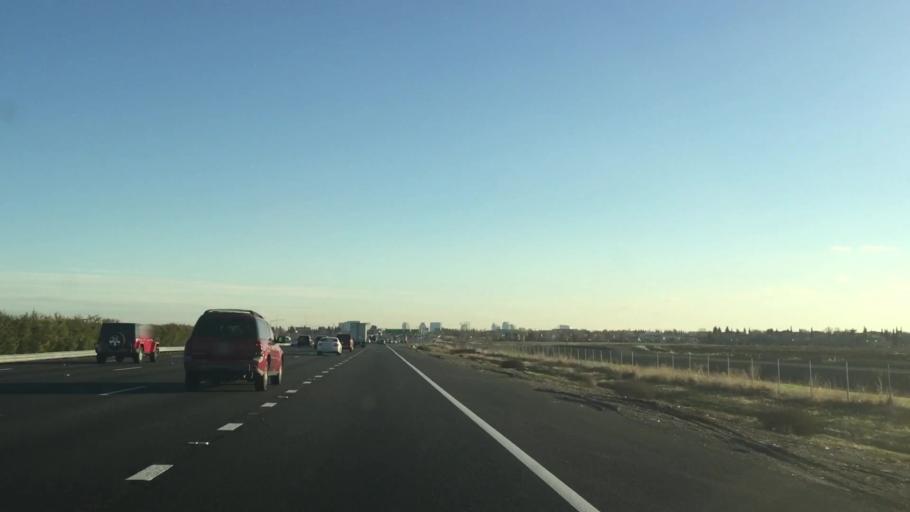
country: US
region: California
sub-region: Yolo County
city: West Sacramento
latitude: 38.6356
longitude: -121.5248
